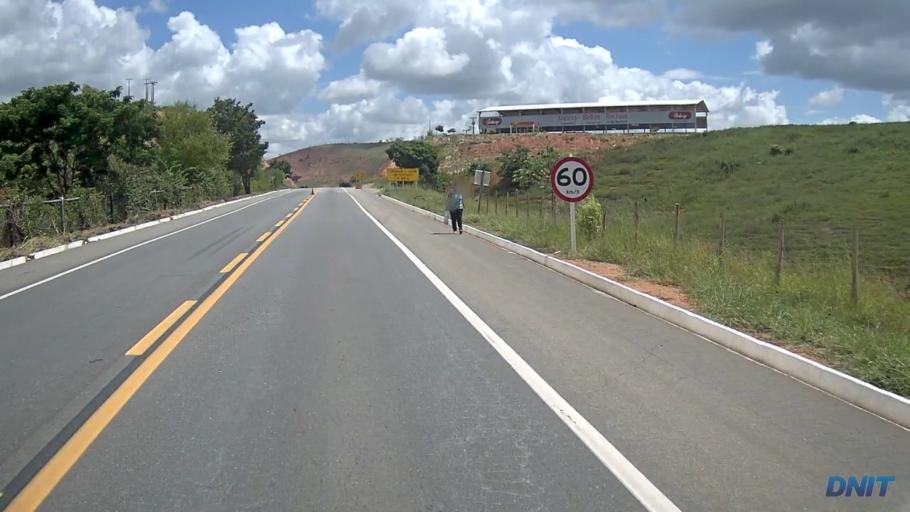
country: BR
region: Minas Gerais
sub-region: Governador Valadares
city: Governador Valadares
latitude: -18.8978
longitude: -42.0042
